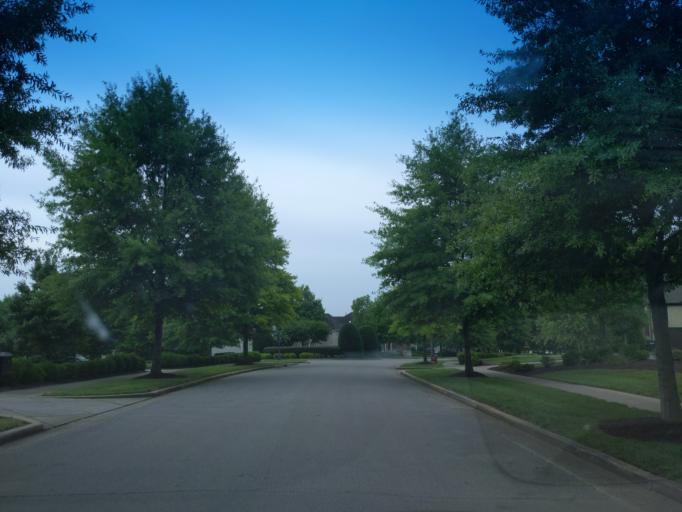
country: US
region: Tennessee
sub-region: Williamson County
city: Brentwood Estates
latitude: 36.0280
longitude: -86.7713
